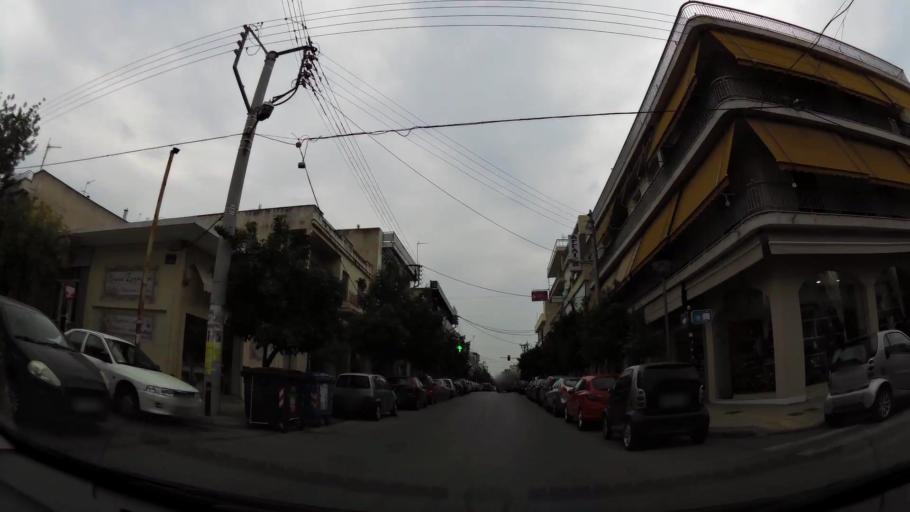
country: GR
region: Attica
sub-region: Nomarchia Athinas
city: Aigaleo
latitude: 37.9908
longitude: 23.6811
